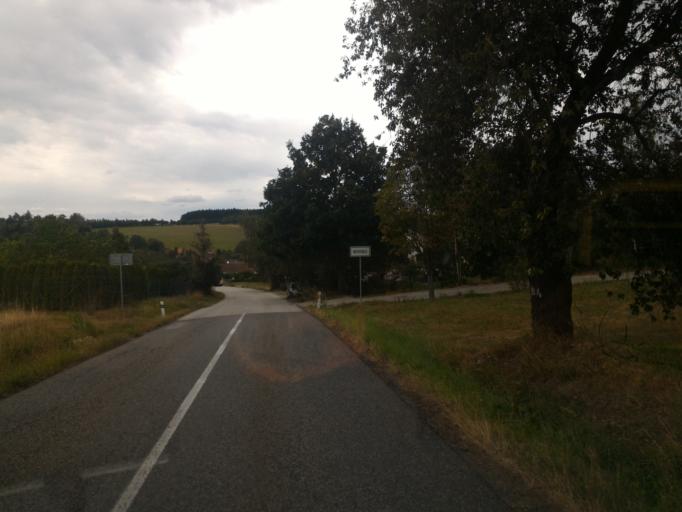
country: CZ
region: Vysocina
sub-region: Okres Jihlava
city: Trest'
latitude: 49.2291
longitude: 15.5380
